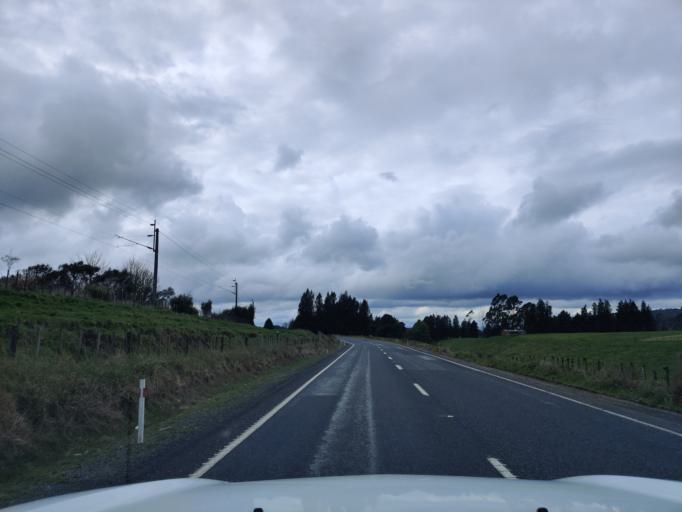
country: NZ
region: Waikato
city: Turangi
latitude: -39.0297
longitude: 175.3820
